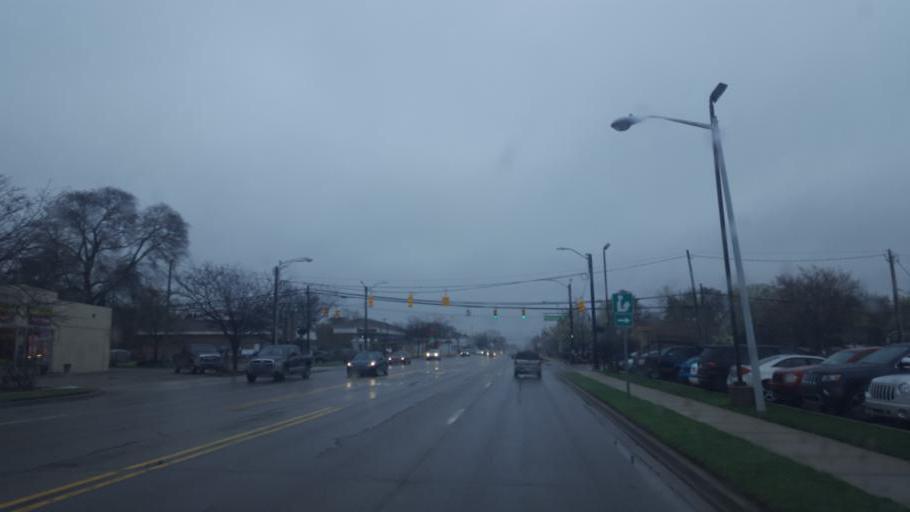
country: US
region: Michigan
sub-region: Isabella County
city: Mount Pleasant
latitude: 43.6043
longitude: -84.7678
